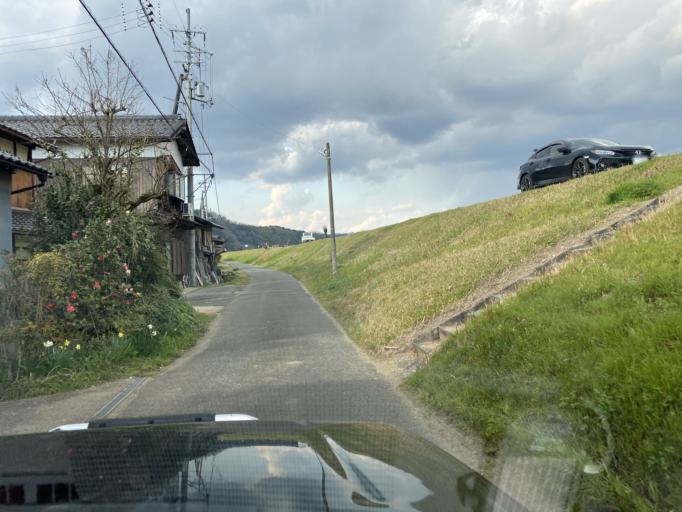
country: JP
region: Hyogo
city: Toyooka
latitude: 35.4955
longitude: 134.8076
